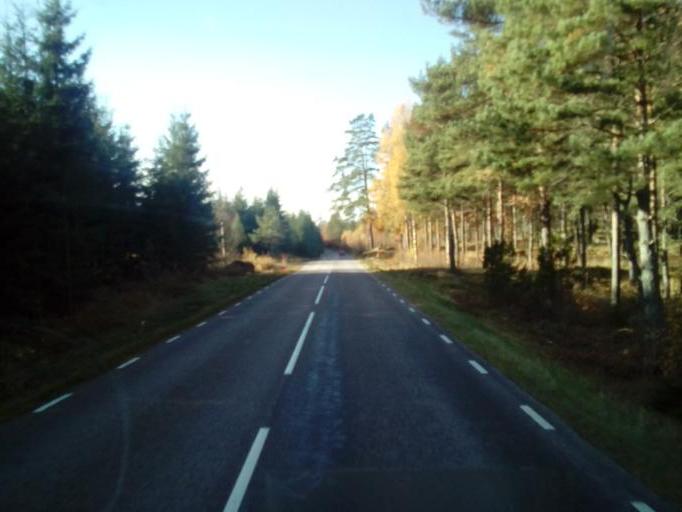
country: SE
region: Kalmar
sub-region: Vasterviks Kommun
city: Ankarsrum
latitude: 57.7882
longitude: 16.1800
